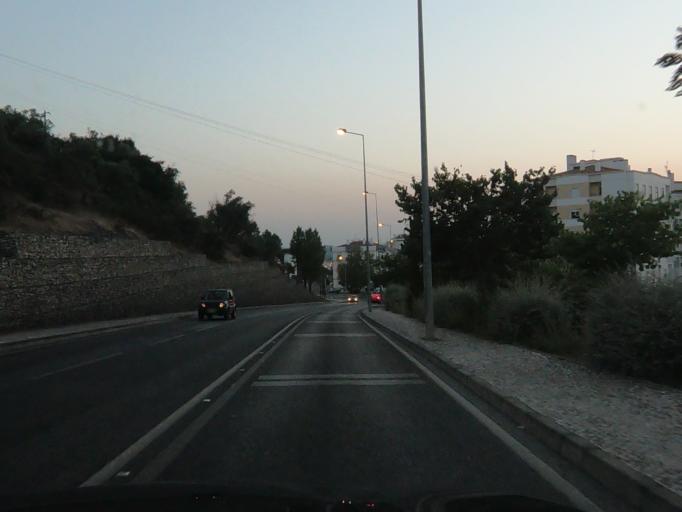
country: PT
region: Santarem
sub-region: Santarem
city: Santarem
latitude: 39.2375
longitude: -8.6938
